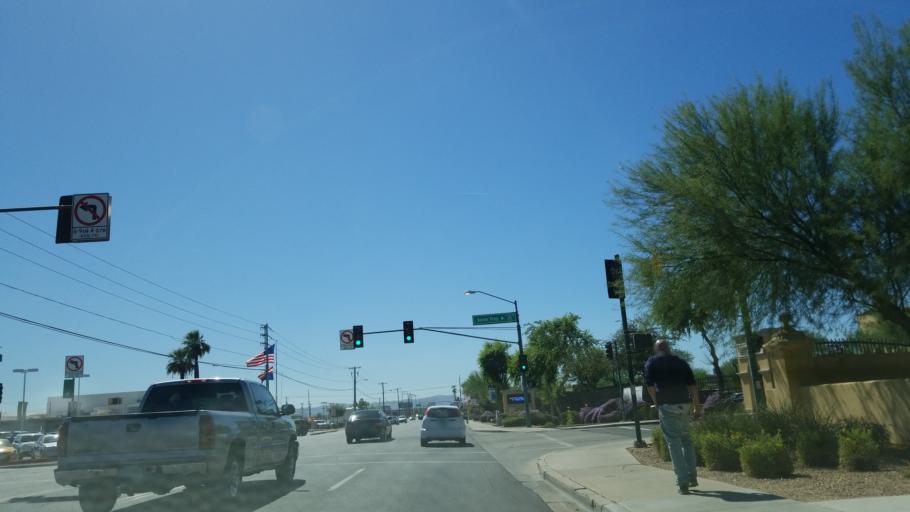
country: US
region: Arizona
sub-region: Maricopa County
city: Phoenix
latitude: 33.5061
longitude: -112.0651
